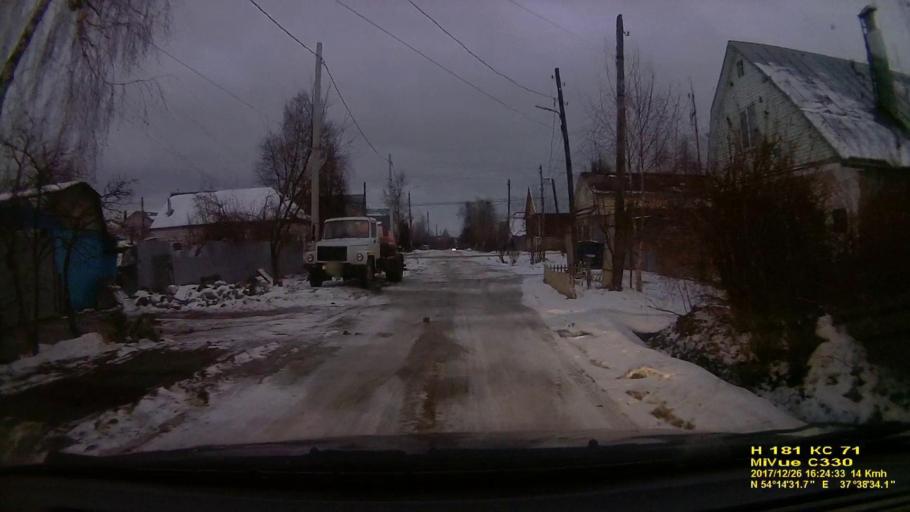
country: RU
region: Tula
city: Gorelki
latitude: 54.2421
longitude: 37.6428
